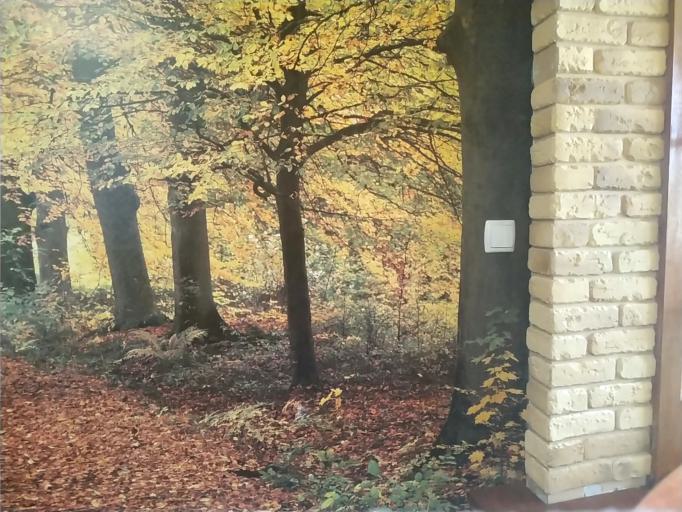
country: RU
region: Tverskaya
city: Vyshniy Volochek
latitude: 57.6614
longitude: 34.5395
